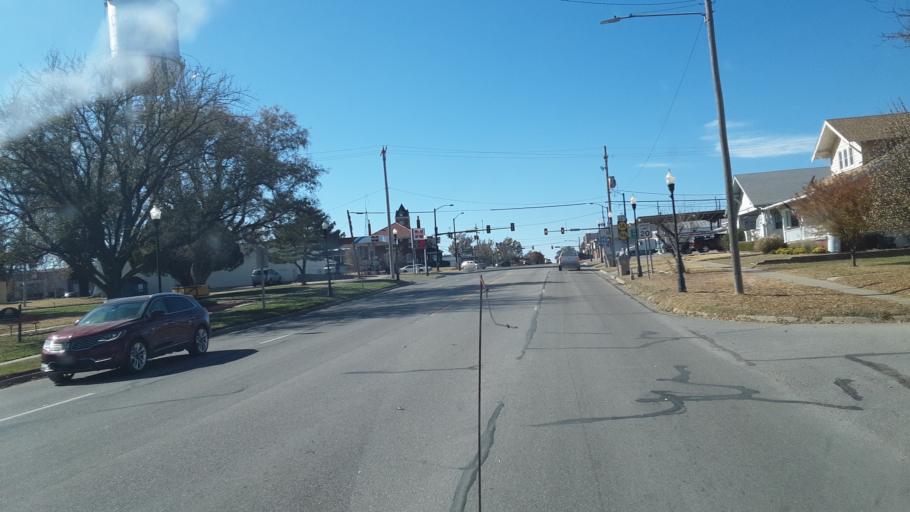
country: US
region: Kansas
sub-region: Rice County
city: Lyons
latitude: 38.3478
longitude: -98.2003
